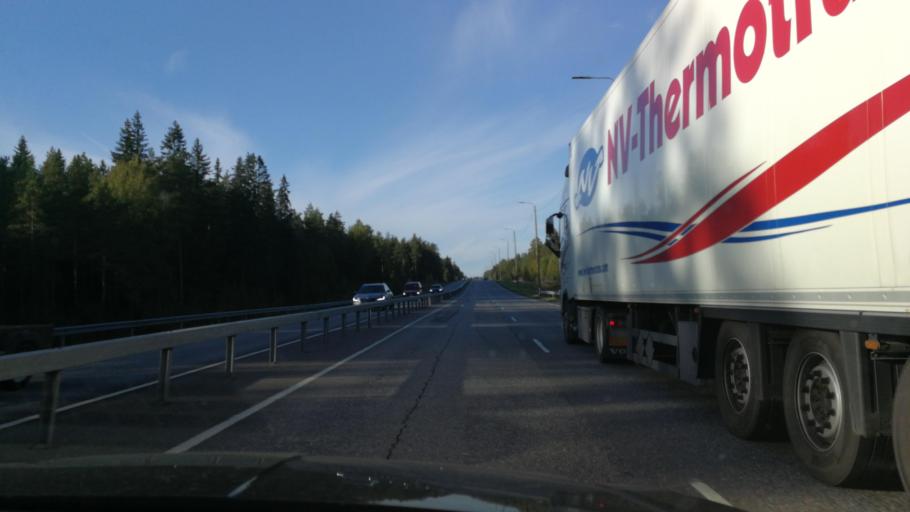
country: FI
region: Varsinais-Suomi
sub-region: Vakka-Suomi
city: Pyhaeranta
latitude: 61.0002
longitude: 21.5715
